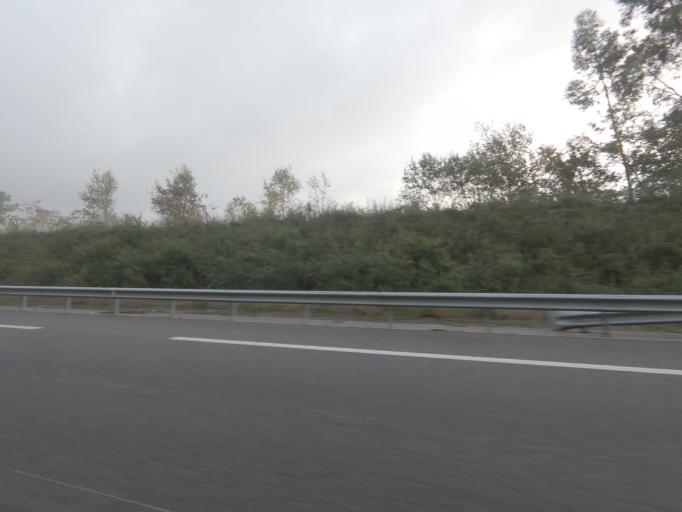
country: ES
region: Galicia
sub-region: Provincia de Pontevedra
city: Porrino
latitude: 42.1860
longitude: -8.6512
